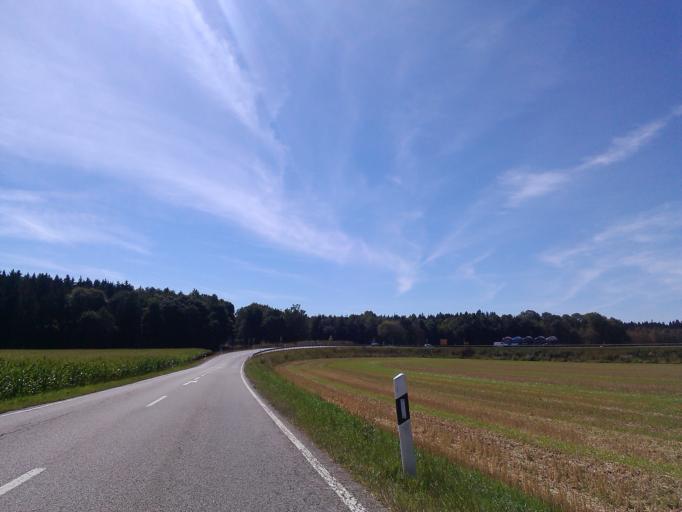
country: DE
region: Bavaria
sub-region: Upper Bavaria
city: Starnberg
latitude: 48.0437
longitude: 11.3160
